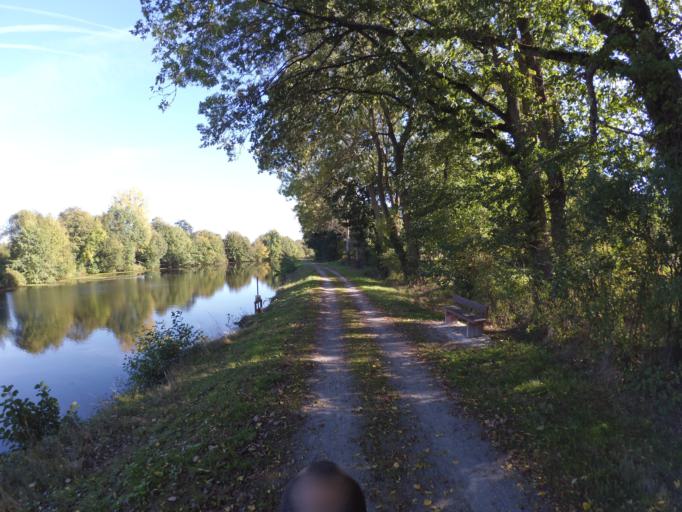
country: FR
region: Brittany
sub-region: Departement du Morbihan
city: Peillac
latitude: 47.7335
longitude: -2.2240
